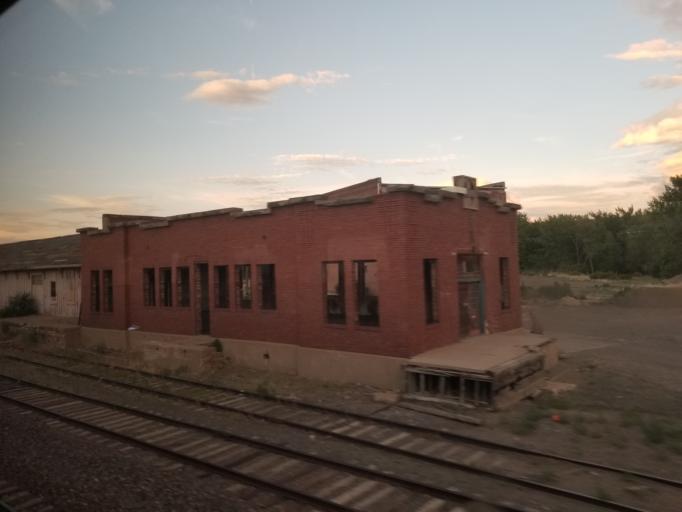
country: US
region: Colorado
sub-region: Las Animas County
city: Trinidad
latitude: 37.1730
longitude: -104.5072
